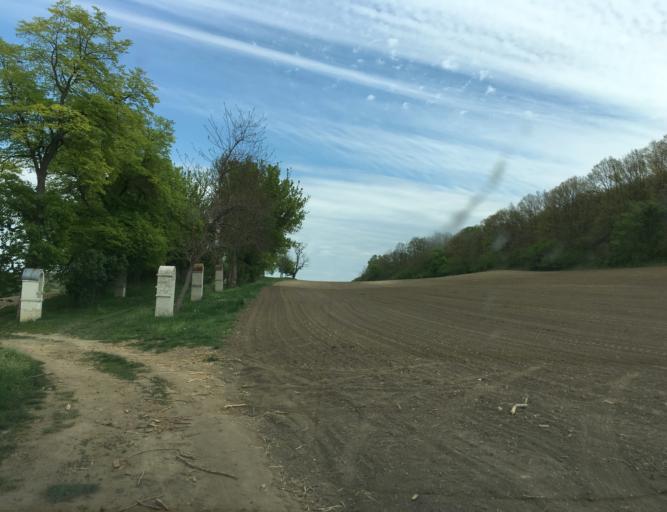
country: SK
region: Nitriansky
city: Svodin
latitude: 47.9234
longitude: 18.4190
